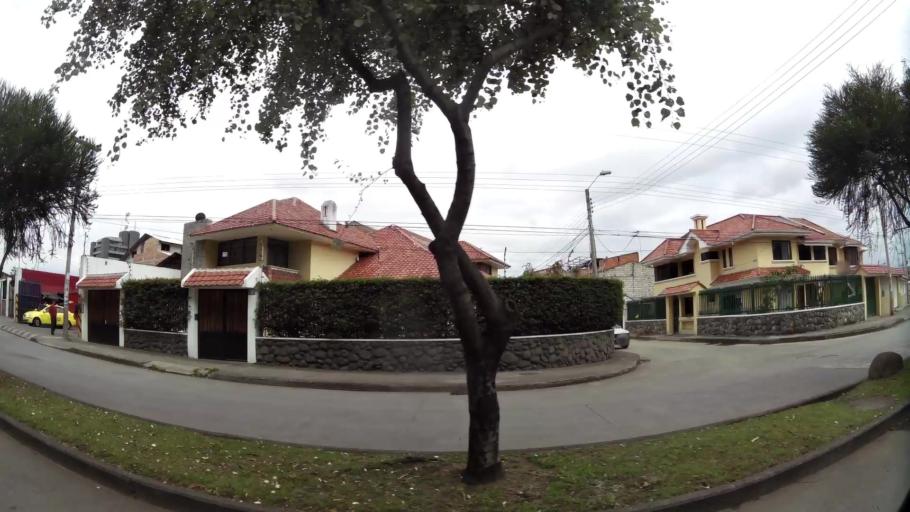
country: EC
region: Azuay
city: Cuenca
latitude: -2.9050
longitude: -78.9816
